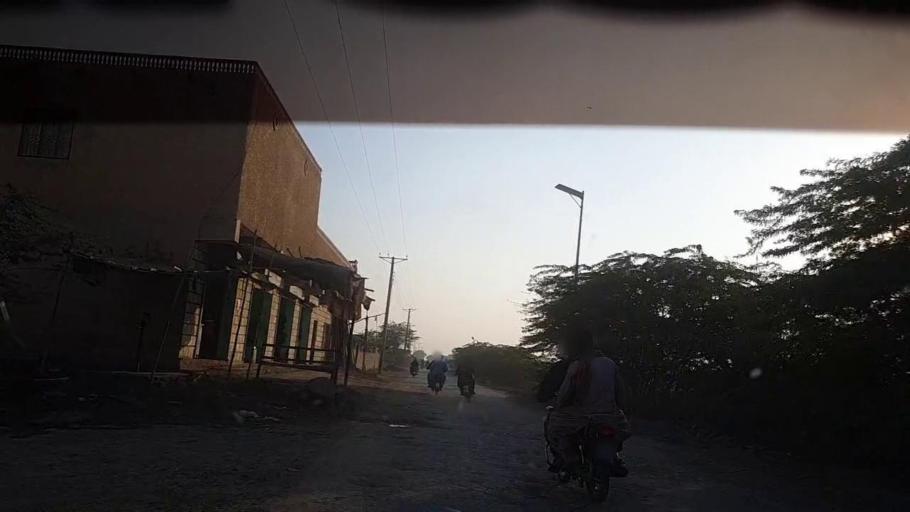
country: PK
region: Sindh
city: Ranipur
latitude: 27.2781
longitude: 68.5149
